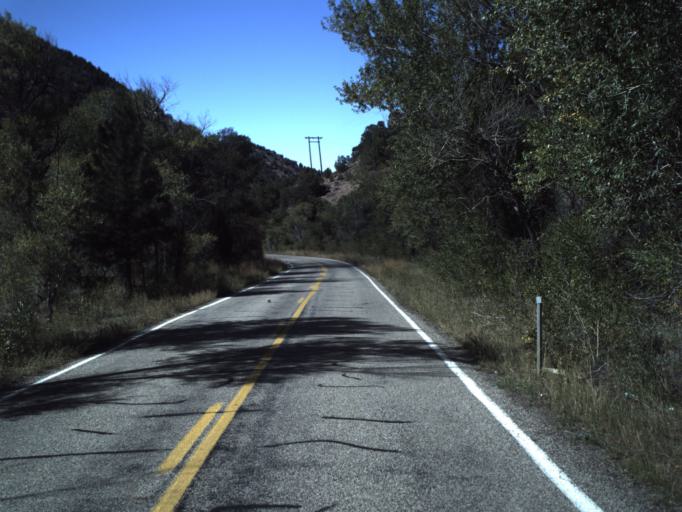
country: US
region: Utah
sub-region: Beaver County
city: Beaver
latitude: 38.2586
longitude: -112.5438
